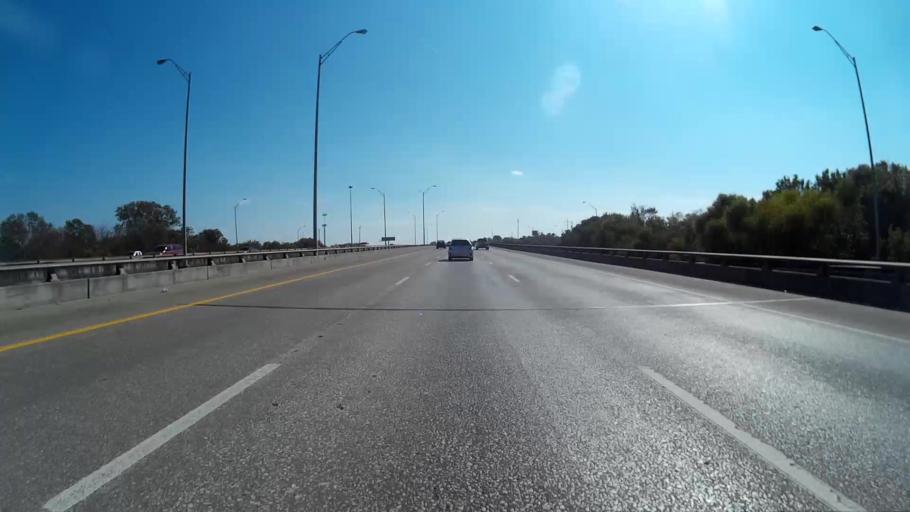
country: US
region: Texas
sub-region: Dallas County
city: Dallas
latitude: 32.7265
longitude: -96.7627
